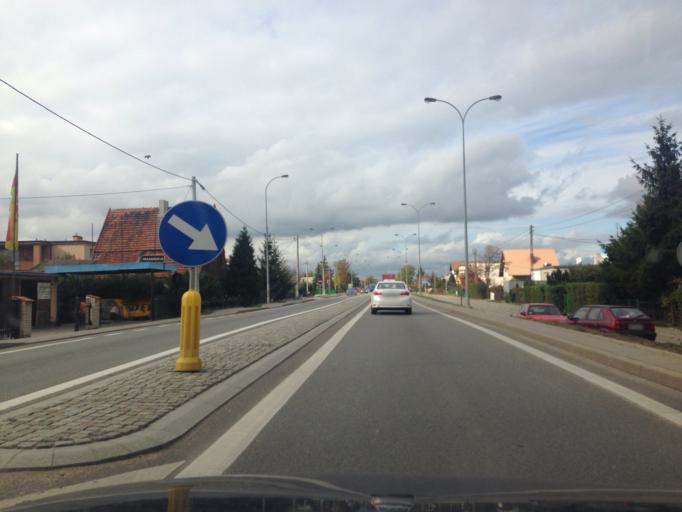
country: PL
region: Pomeranian Voivodeship
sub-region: Powiat gdanski
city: Pszczolki
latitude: 54.1749
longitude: 18.6916
